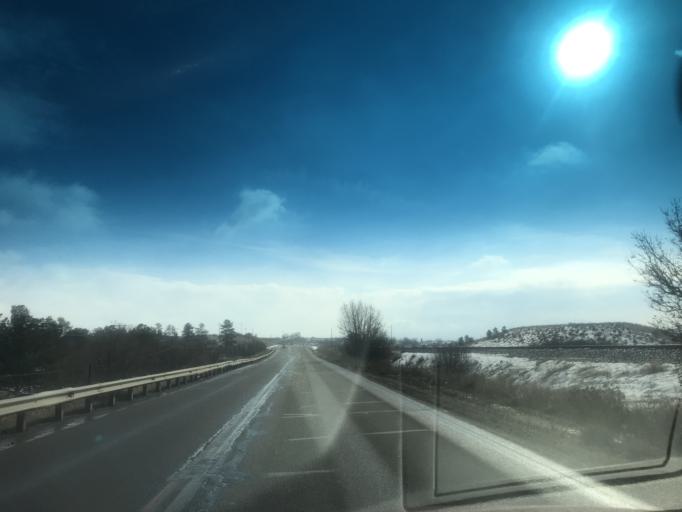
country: US
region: Colorado
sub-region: Douglas County
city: Castle Pines
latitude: 39.4549
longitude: -104.9804
